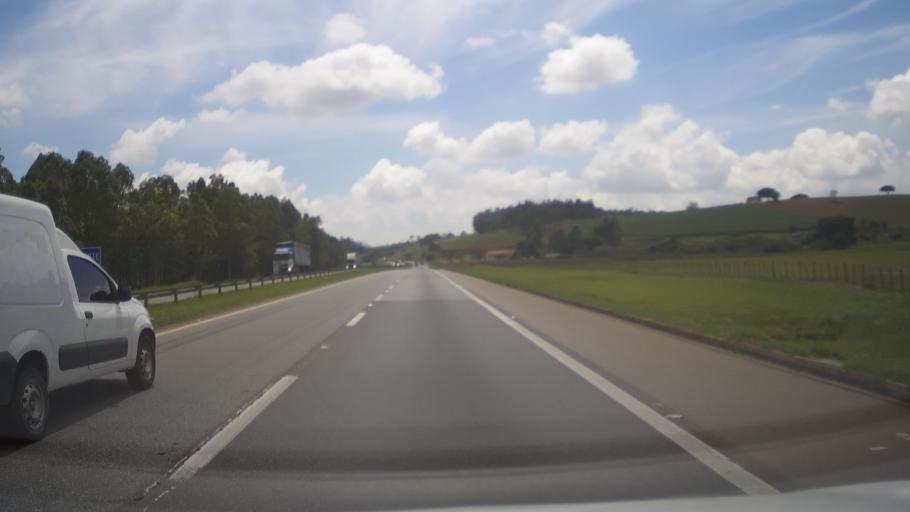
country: BR
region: Minas Gerais
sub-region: Santa Rita Do Sapucai
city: Santa Rita do Sapucai
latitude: -22.0968
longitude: -45.7160
